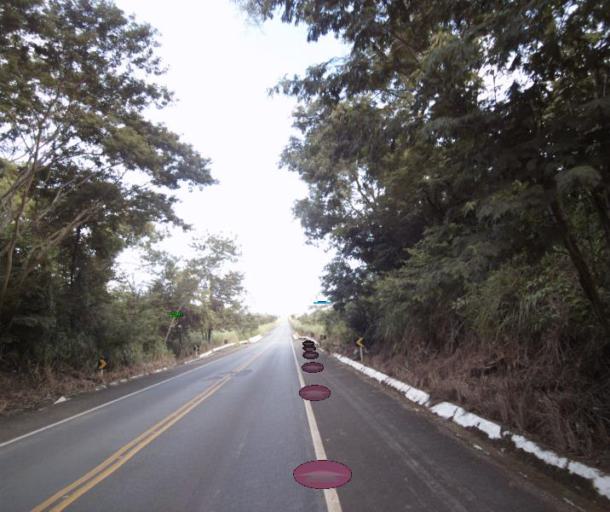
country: BR
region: Goias
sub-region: Niquelandia
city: Niquelandia
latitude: -14.7327
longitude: -48.6134
